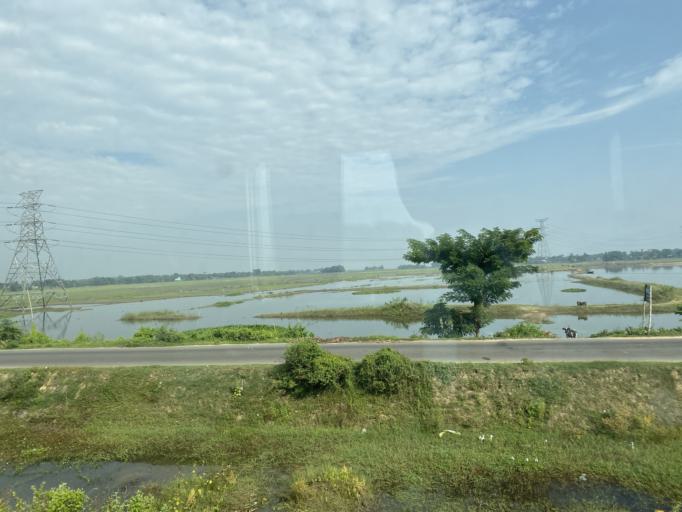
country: IN
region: Tripura
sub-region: West Tripura
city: Agartala
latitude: 23.8798
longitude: 91.1962
